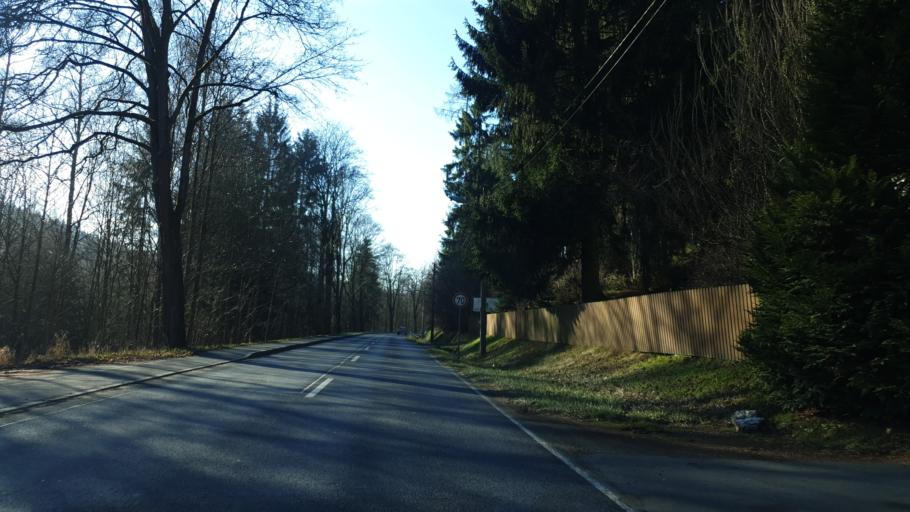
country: DE
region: Saxony
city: Bad Elster
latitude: 50.2957
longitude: 12.2472
